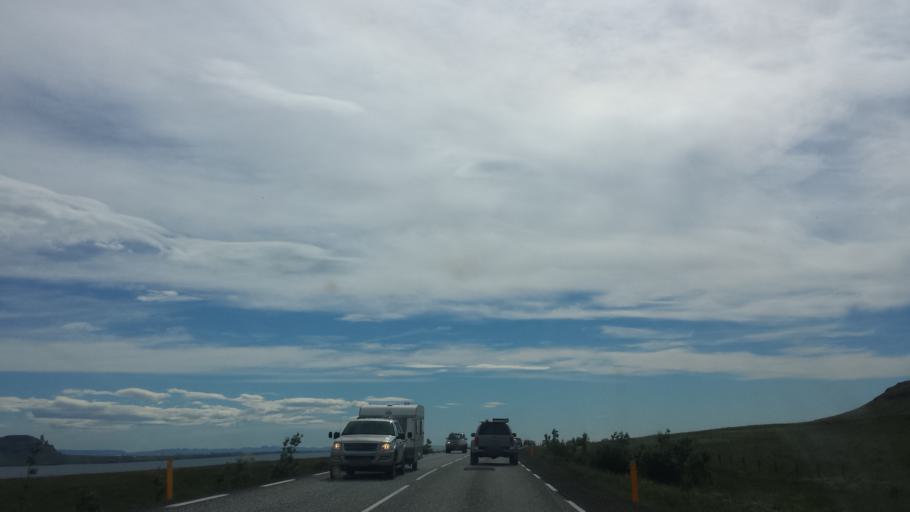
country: IS
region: Capital Region
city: Mosfellsbaer
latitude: 64.3440
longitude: -21.8171
